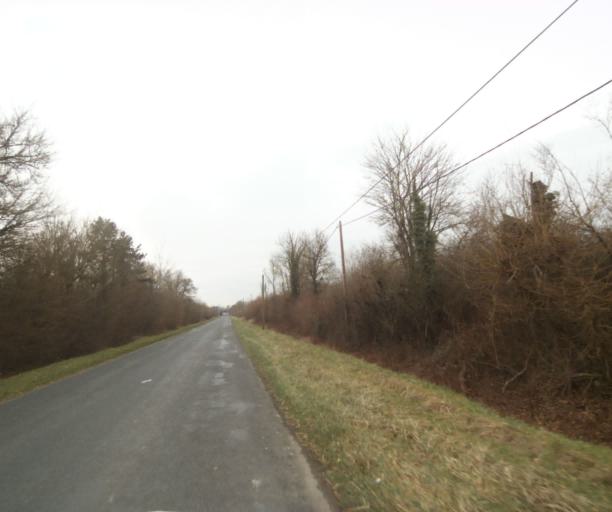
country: FR
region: Champagne-Ardenne
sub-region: Departement de la Haute-Marne
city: Villiers-en-Lieu
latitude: 48.6520
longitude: 4.8754
